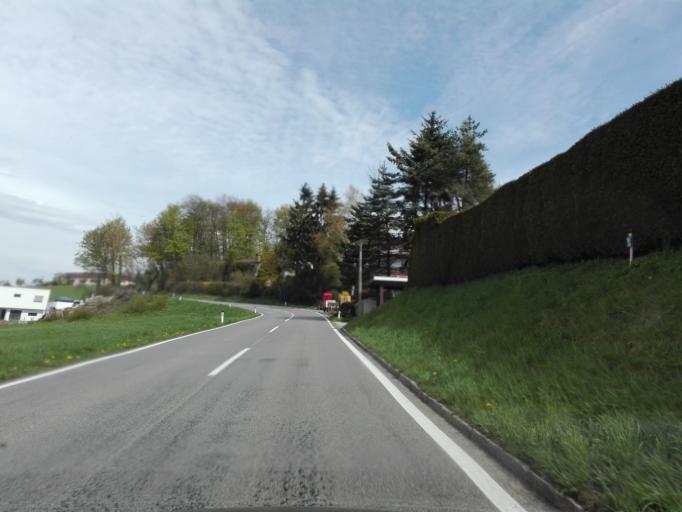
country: AT
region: Upper Austria
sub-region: Politischer Bezirk Urfahr-Umgebung
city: Eidenberg
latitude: 48.3528
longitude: 14.2393
